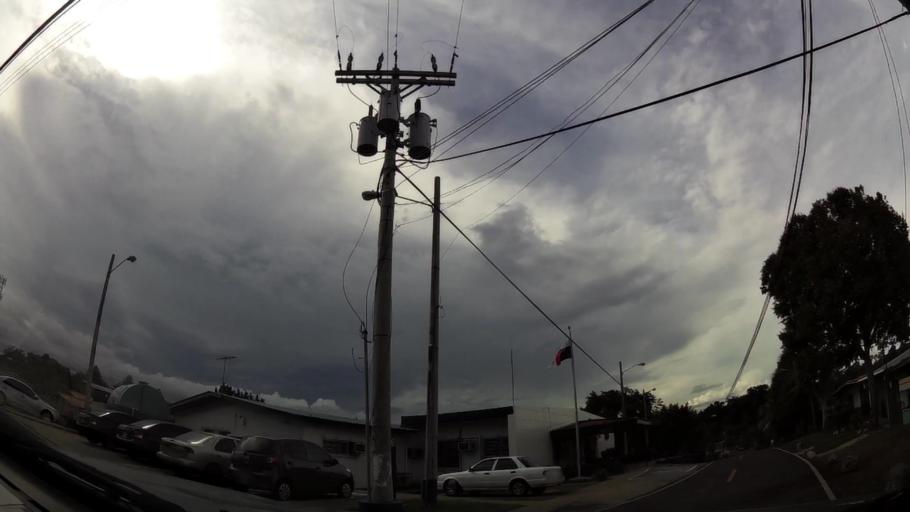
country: PA
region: Panama
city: El Coco
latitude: 8.8650
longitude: -79.8104
